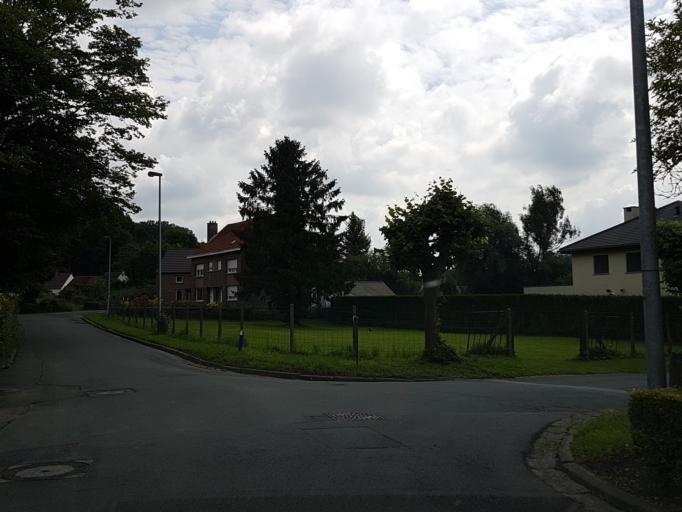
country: BE
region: Flanders
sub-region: Provincie Oost-Vlaanderen
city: Denderleeuw
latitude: 50.9079
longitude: 4.1105
